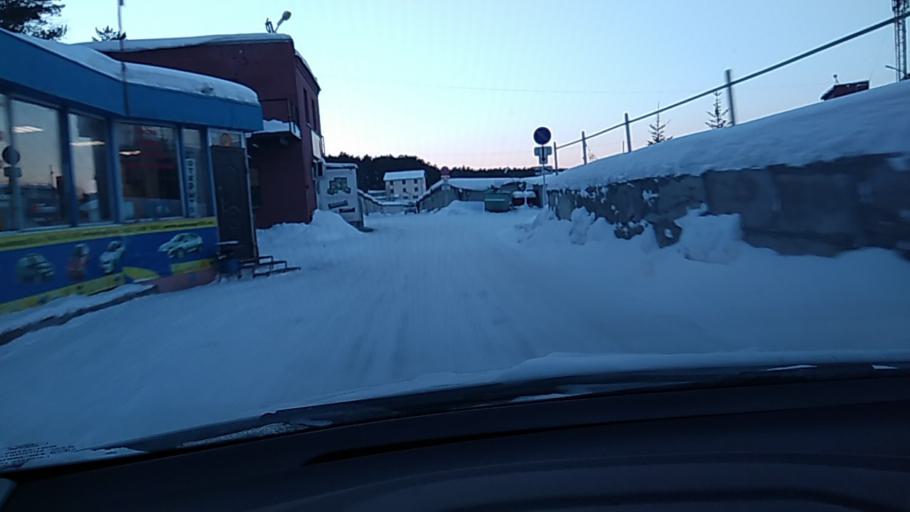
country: RU
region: Sverdlovsk
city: Sovkhoznyy
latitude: 56.7923
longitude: 60.5671
